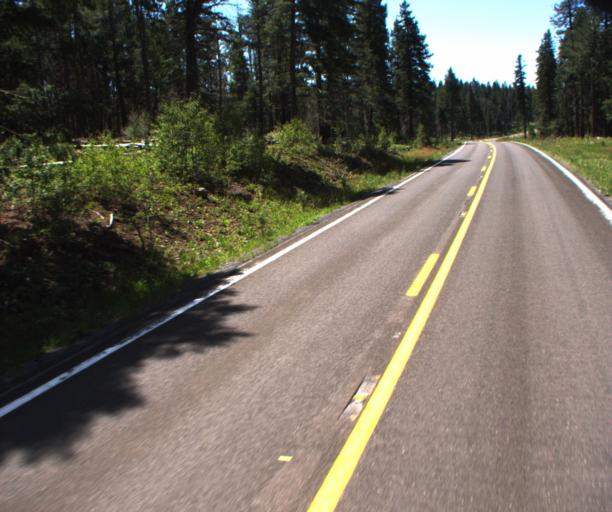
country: US
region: Arizona
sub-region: Apache County
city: Eagar
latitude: 33.6269
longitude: -109.3274
